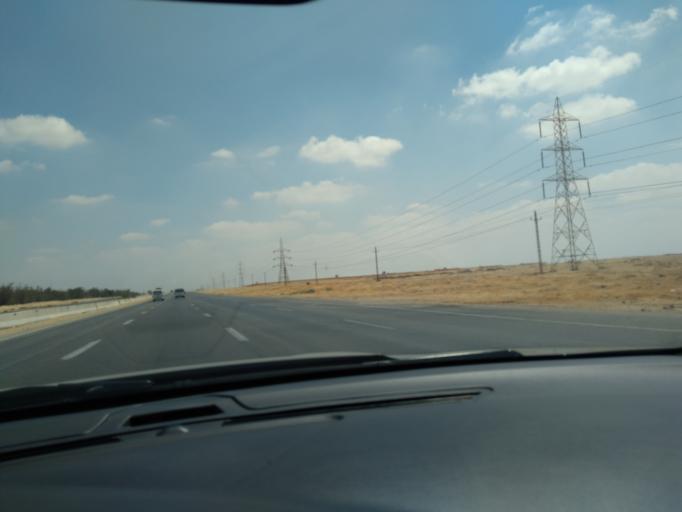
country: EG
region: Al Isma'iliyah
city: At Tall al Kabir
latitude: 30.3934
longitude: 31.9715
